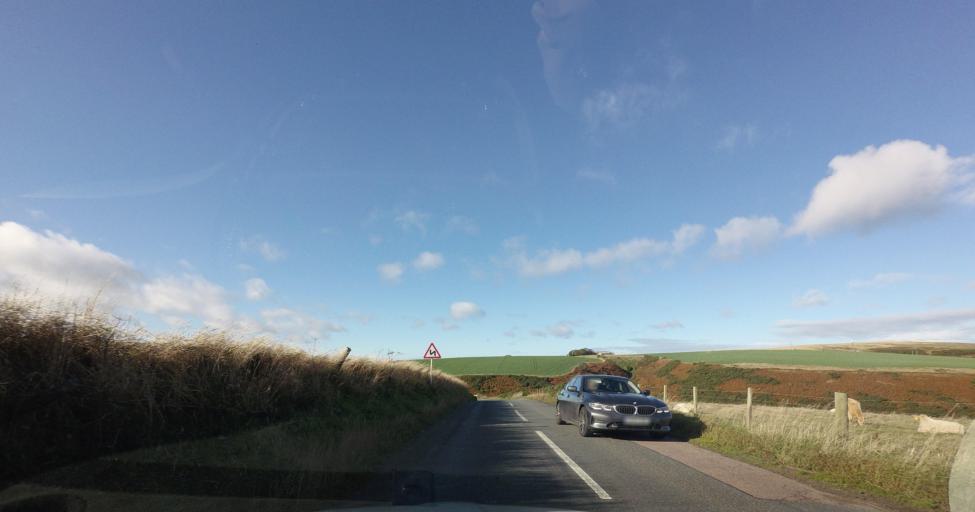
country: GB
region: Scotland
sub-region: Aberdeenshire
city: Macduff
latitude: 57.6615
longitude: -2.3527
